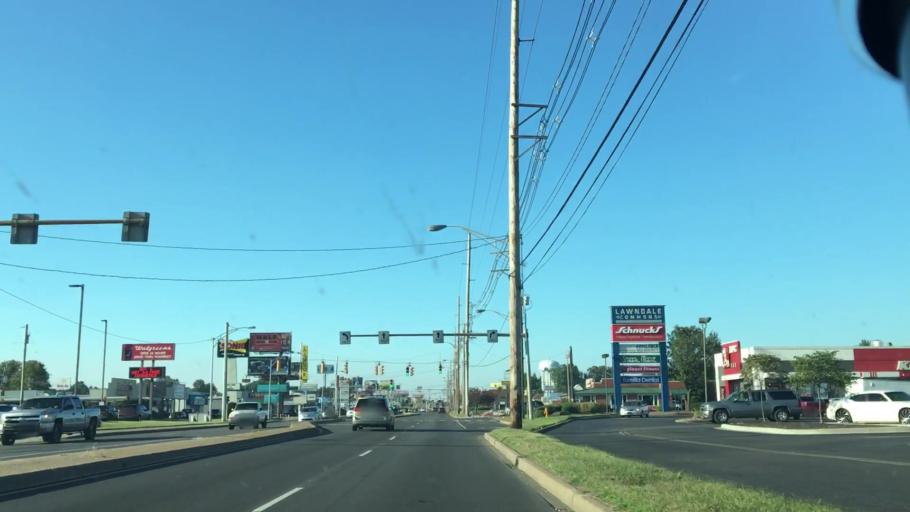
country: US
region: Indiana
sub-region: Vanderburgh County
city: Evansville
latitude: 37.9632
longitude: -87.4926
